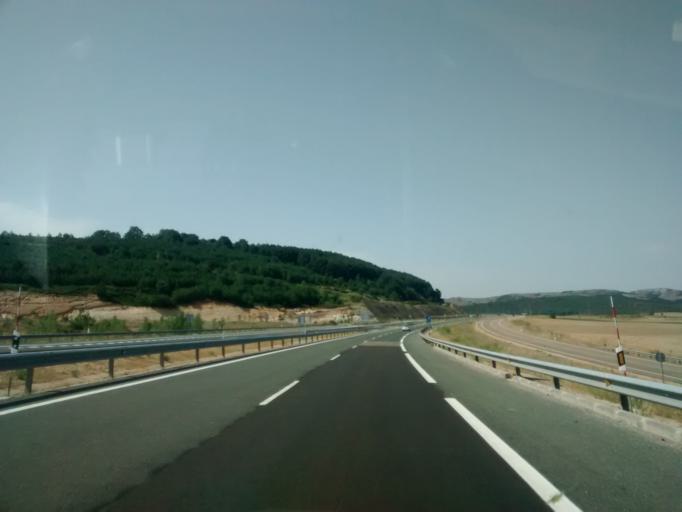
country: ES
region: Castille and Leon
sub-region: Provincia de Palencia
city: Aguilar de Campoo
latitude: 42.7637
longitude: -4.2830
